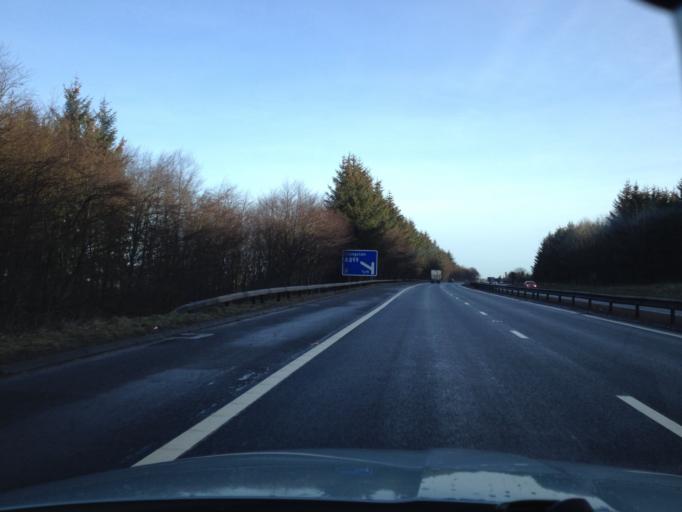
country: GB
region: Scotland
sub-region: West Lothian
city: Livingston
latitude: 55.9141
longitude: -3.5545
